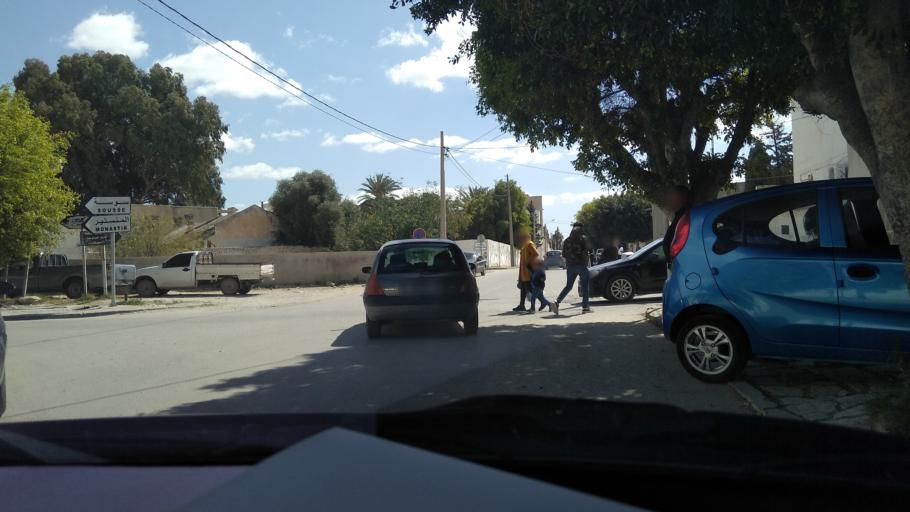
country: TN
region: Al Qayrawan
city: Kairouan
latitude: 35.6720
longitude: 10.1046
